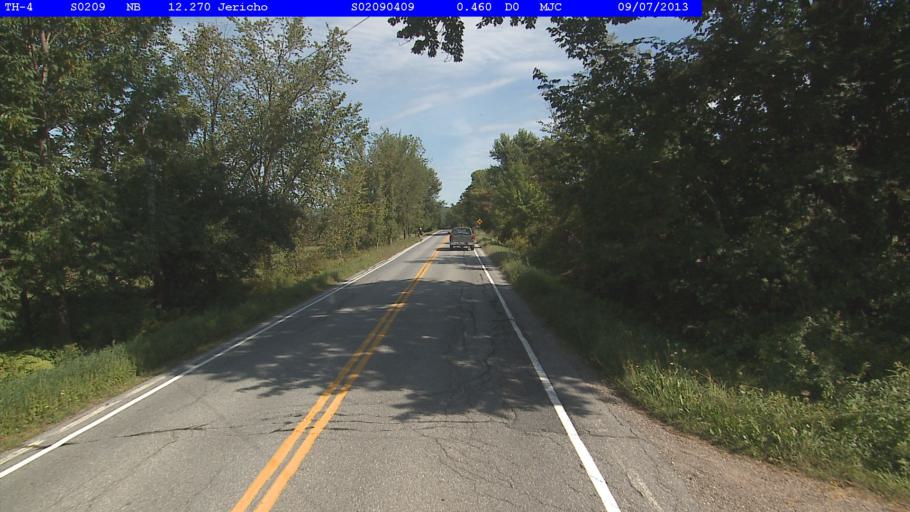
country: US
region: Vermont
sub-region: Chittenden County
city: Jericho
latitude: 44.4379
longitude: -72.9789
